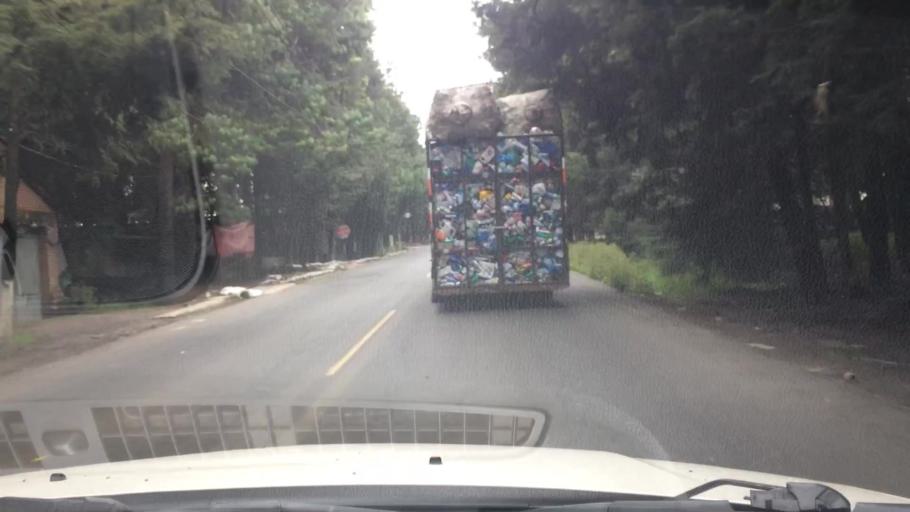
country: MX
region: Mexico City
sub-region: Tlalpan
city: Lomas de Tepemecatl
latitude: 19.2402
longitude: -99.2375
